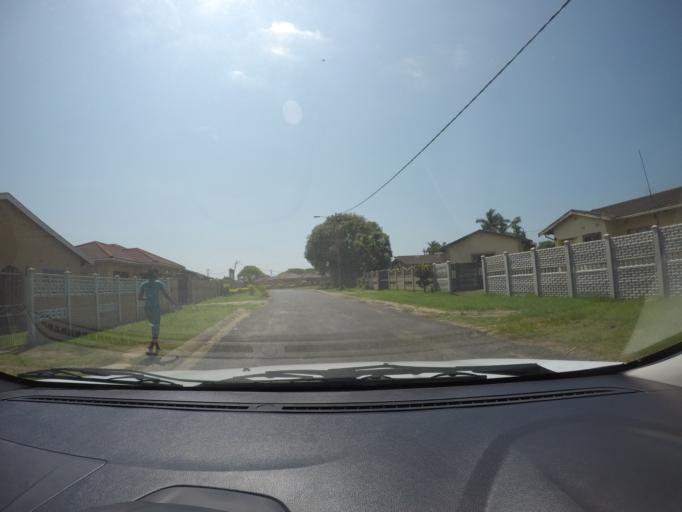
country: ZA
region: KwaZulu-Natal
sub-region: uThungulu District Municipality
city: eSikhawini
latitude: -28.8626
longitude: 31.9225
